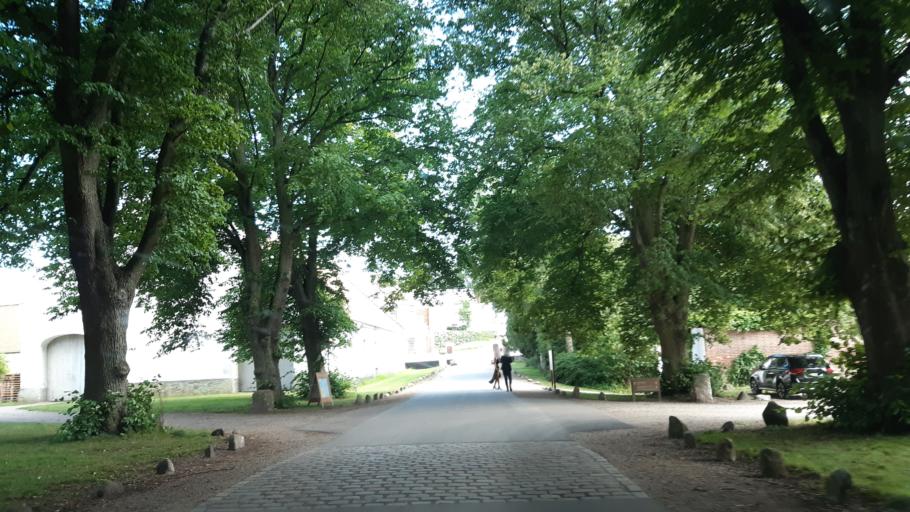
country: DK
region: Zealand
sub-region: Odsherred Kommune
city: Horve
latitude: 55.7730
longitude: 11.3905
